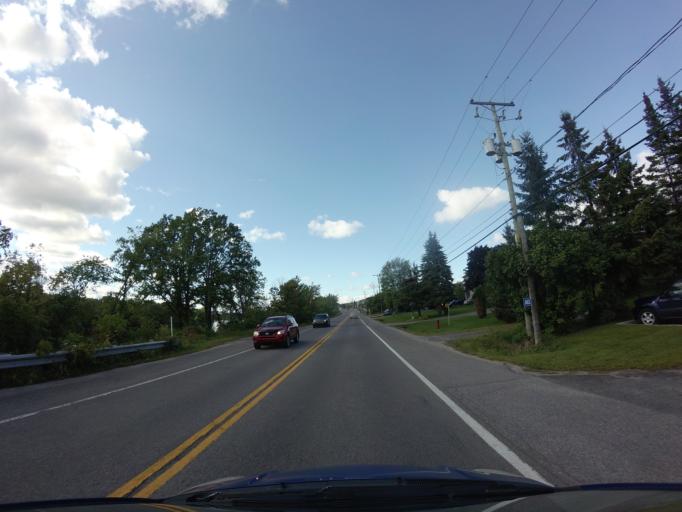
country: CA
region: Quebec
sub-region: Outaouais
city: Gatineau
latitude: 45.4679
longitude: -75.7252
